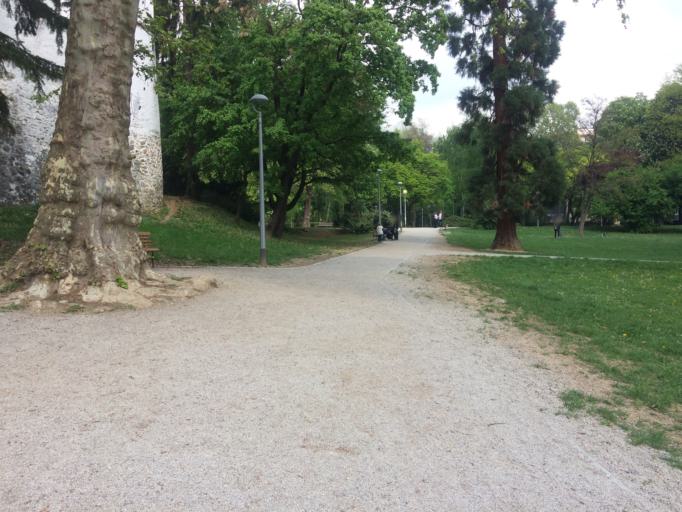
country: HR
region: Grad Zagreb
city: Zagreb
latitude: 45.8154
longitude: 15.9805
